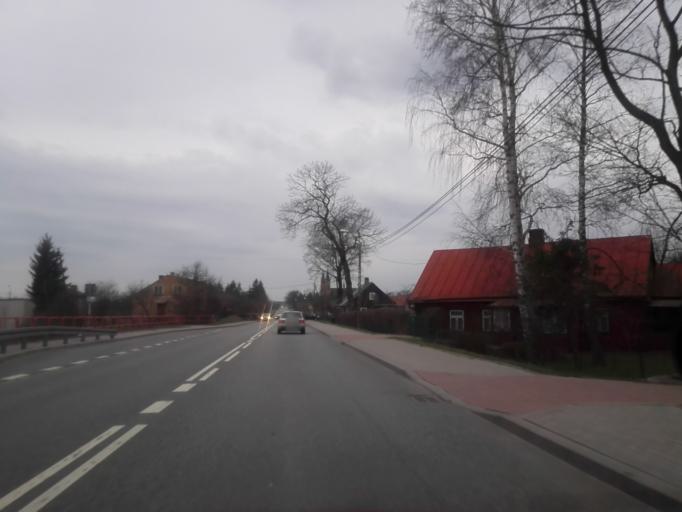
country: PL
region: Podlasie
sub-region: Powiat grajewski
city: Rajgrod
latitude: 53.7313
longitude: 22.7090
